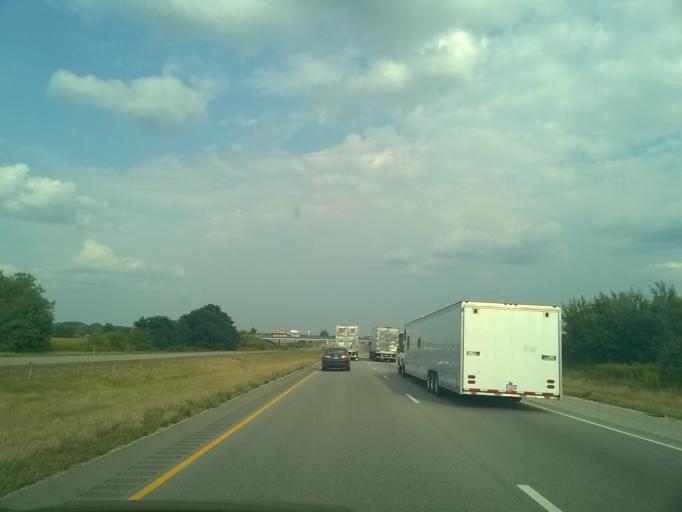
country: US
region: Indiana
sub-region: Clay County
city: Brazil
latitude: 39.4503
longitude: -87.1657
